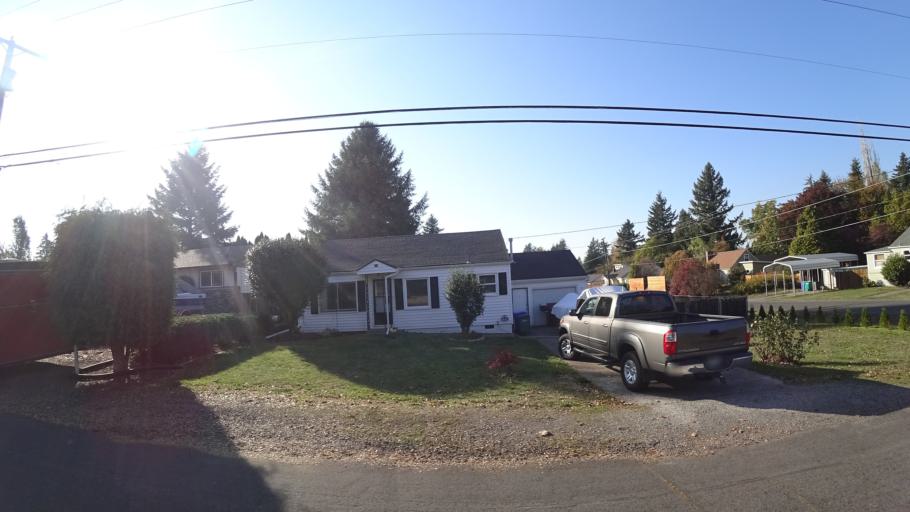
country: US
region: Oregon
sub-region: Multnomah County
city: Fairview
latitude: 45.5208
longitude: -122.4355
